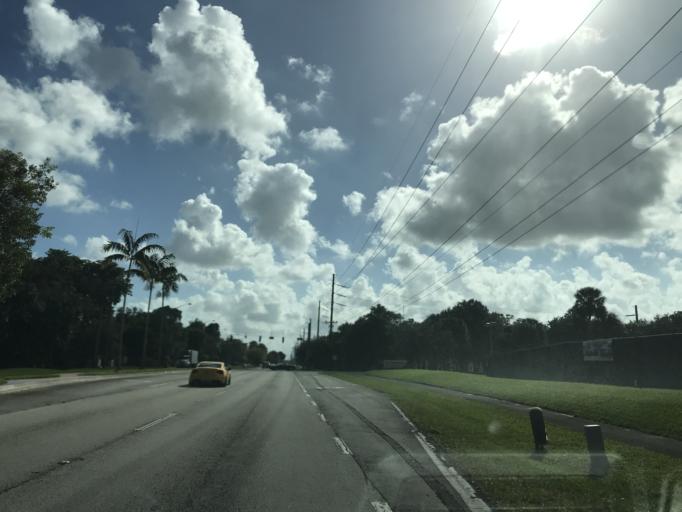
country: US
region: Florida
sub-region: Broward County
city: Coconut Creek
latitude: 26.2579
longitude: -80.1865
